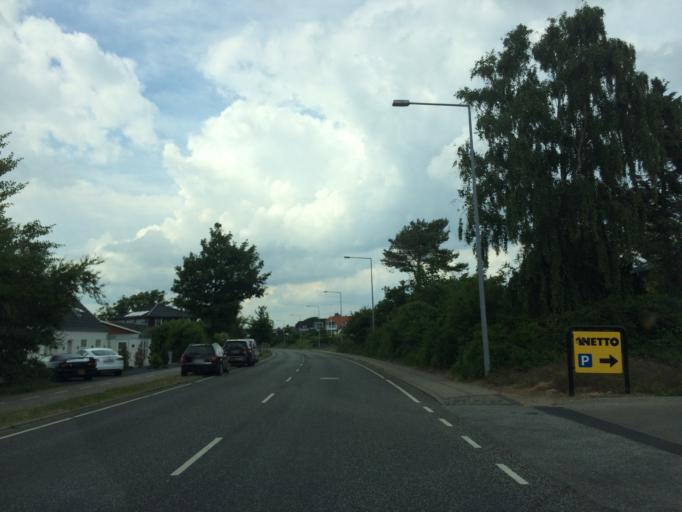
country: DK
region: South Denmark
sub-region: Middelfart Kommune
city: Strib
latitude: 55.5310
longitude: 9.7713
